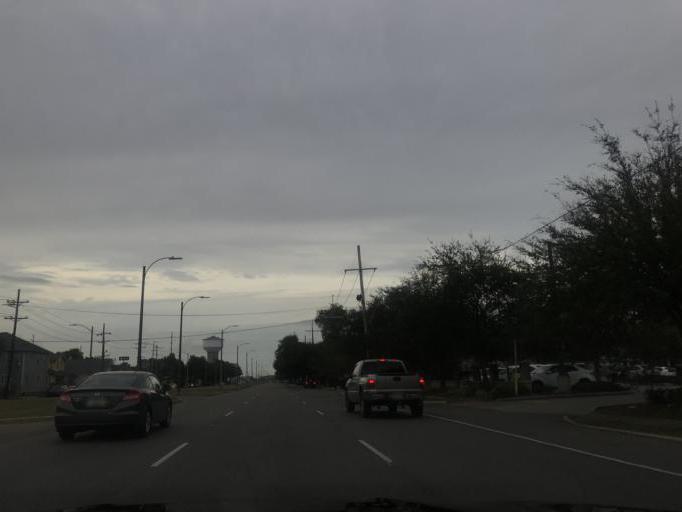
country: US
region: Louisiana
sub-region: Jefferson Parish
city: Jefferson
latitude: 29.9563
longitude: -90.1208
